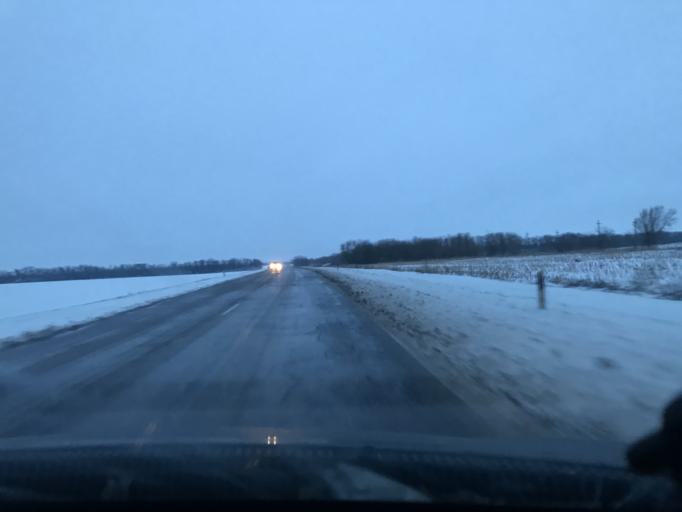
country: RU
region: Rostov
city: Letnik
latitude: 45.9875
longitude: 41.2301
